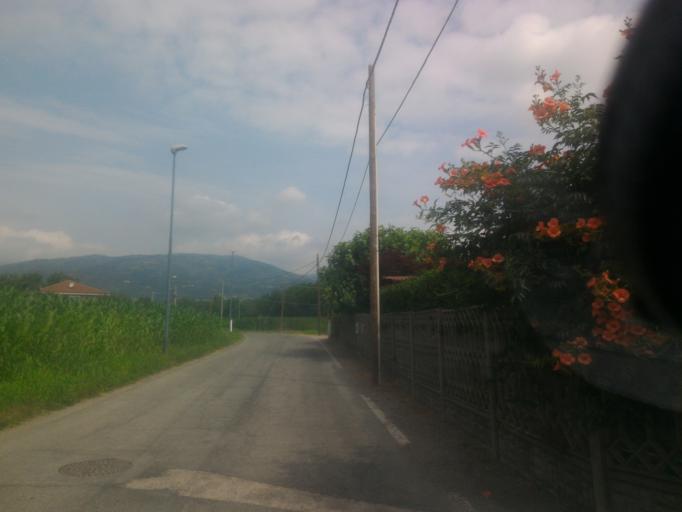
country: IT
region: Piedmont
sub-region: Provincia di Torino
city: Pinerolo
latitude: 44.8699
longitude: 7.3186
